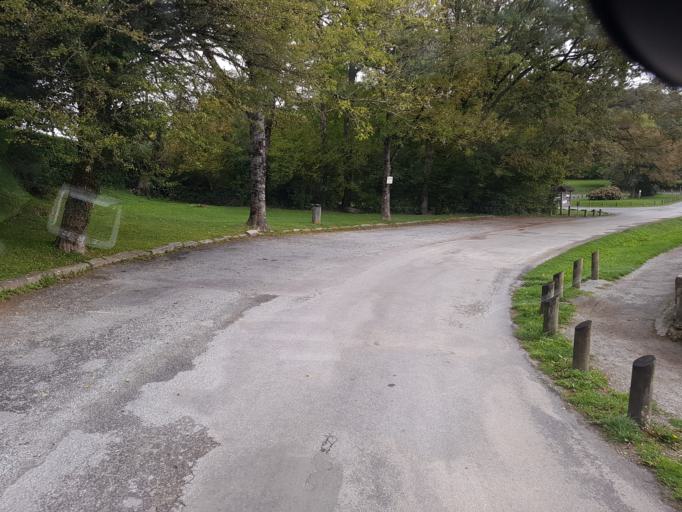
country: FR
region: Midi-Pyrenees
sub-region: Departement du Tarn
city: Mazamet
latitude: 43.4651
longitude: 2.3431
